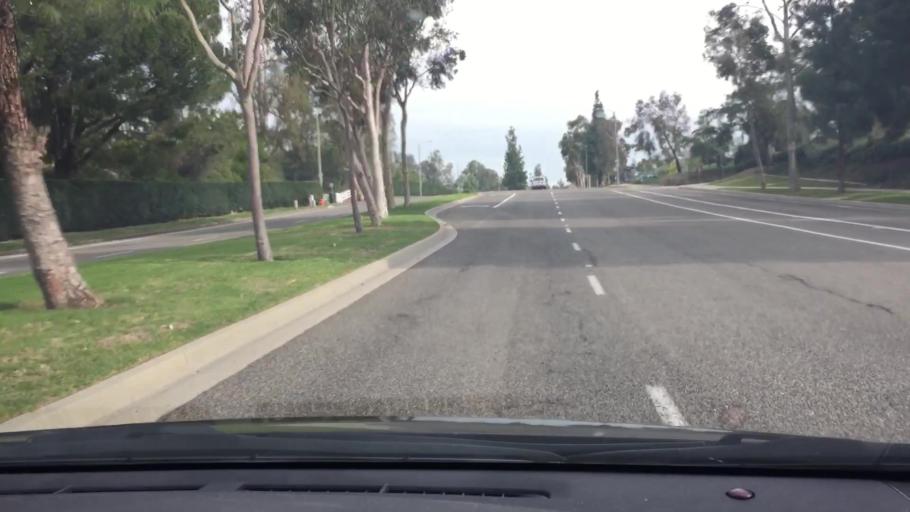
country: US
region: California
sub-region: Orange County
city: North Tustin
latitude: 33.7966
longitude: -117.7702
